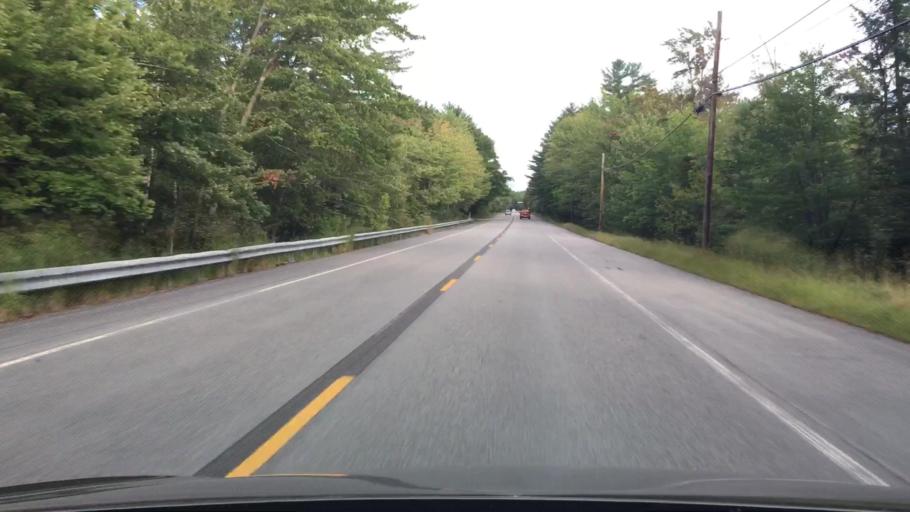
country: US
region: Maine
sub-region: Cumberland County
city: Bridgton
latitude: 44.0655
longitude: -70.7478
